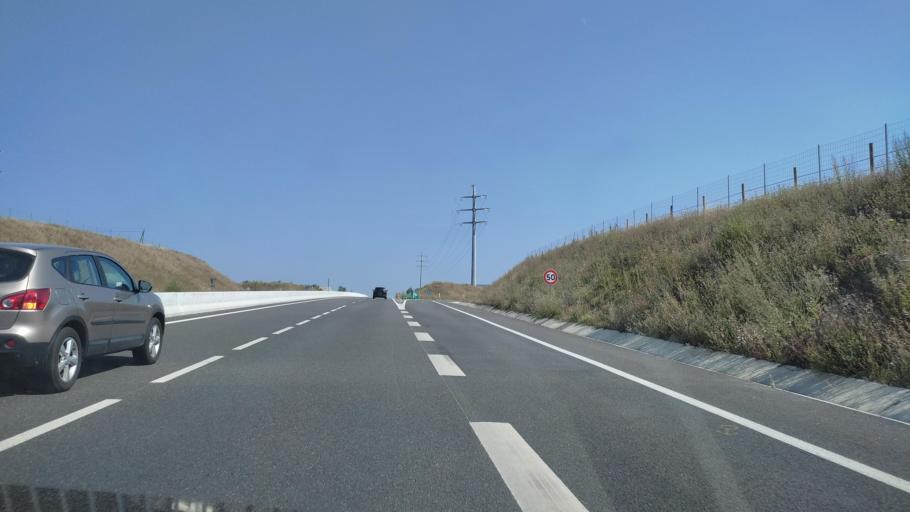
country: FR
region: Poitou-Charentes
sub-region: Departement de la Charente
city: Balzac
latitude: 45.6928
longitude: 0.0979
